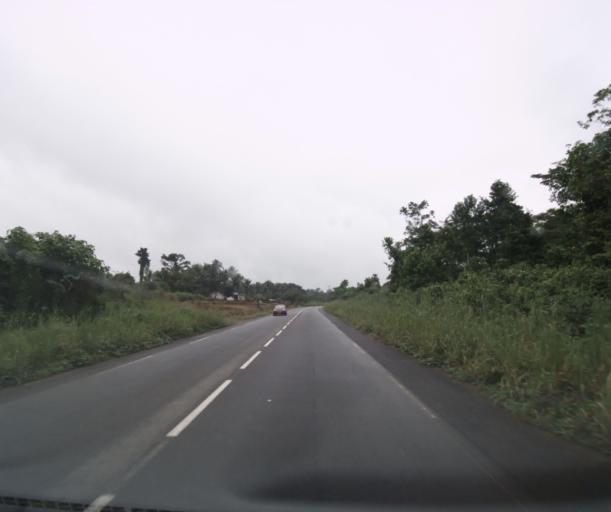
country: CM
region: Littoral
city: Edea
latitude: 3.4768
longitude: 10.1327
